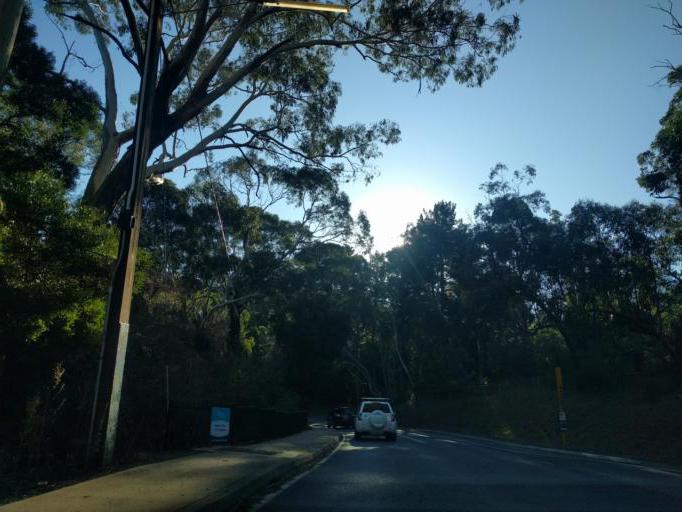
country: AU
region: South Australia
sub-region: Adelaide Hills
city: Aldgate
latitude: -35.0134
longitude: 138.7325
